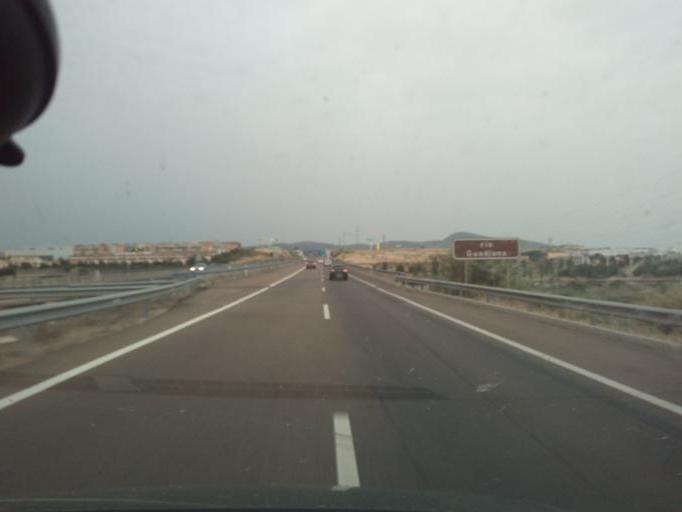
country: ES
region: Extremadura
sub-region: Provincia de Badajoz
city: Merida
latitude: 38.9312
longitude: -6.3675
